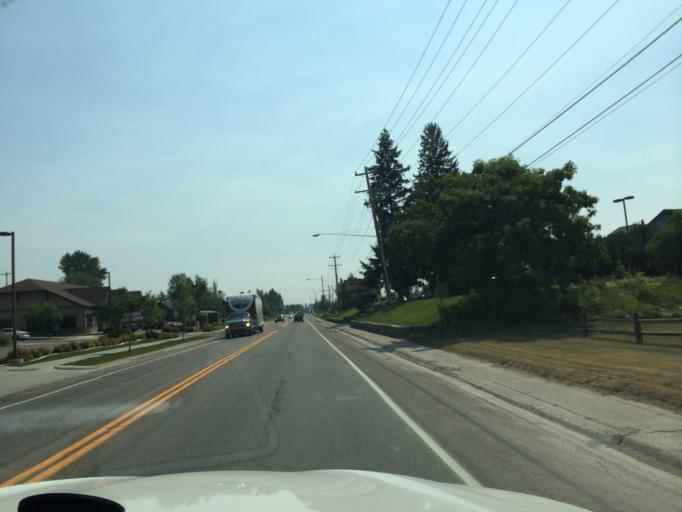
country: US
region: Montana
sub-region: Flathead County
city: Whitefish
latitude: 48.4040
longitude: -114.3353
